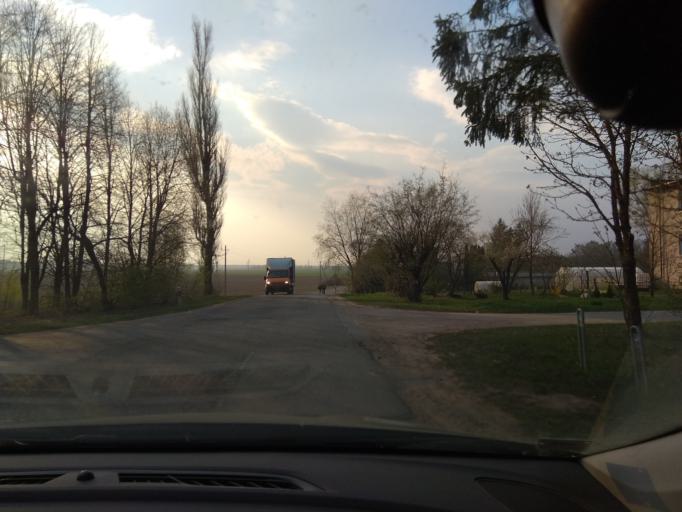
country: LT
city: Baltoji Voke
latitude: 54.5992
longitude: 25.1410
